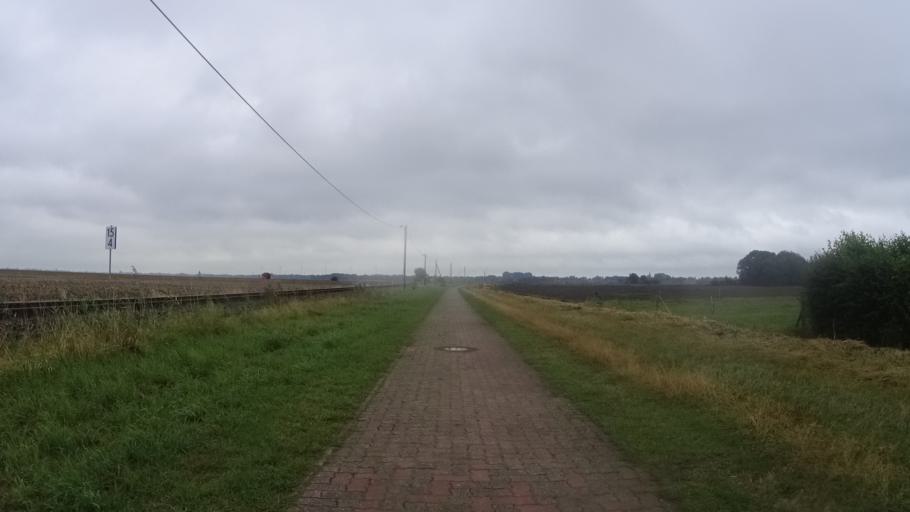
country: DE
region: Lower Saxony
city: Bunde
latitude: 53.1895
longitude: 7.2411
